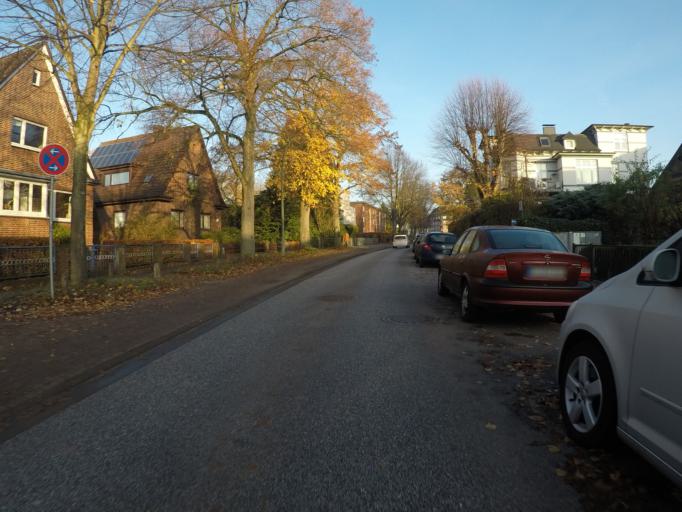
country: DE
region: Hamburg
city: Stellingen
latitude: 53.5947
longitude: 9.9328
